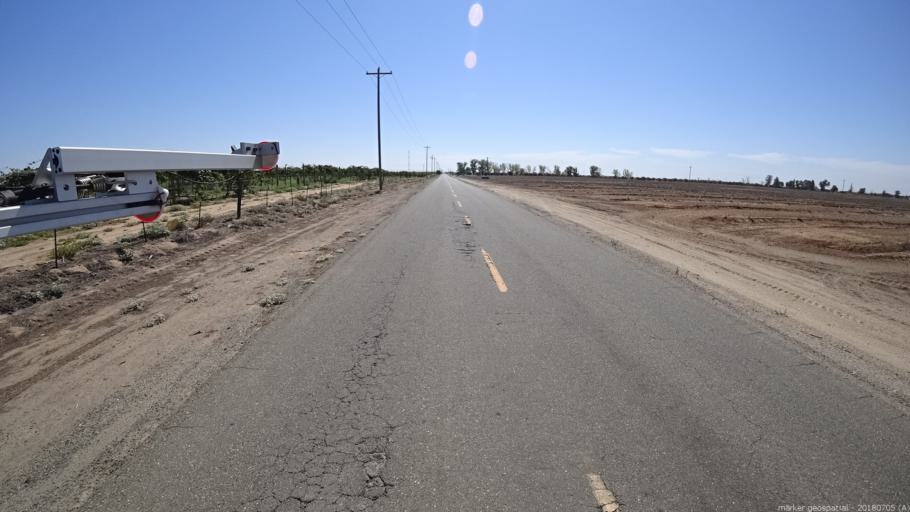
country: US
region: California
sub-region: Madera County
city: Fairmead
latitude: 37.0981
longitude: -120.1359
